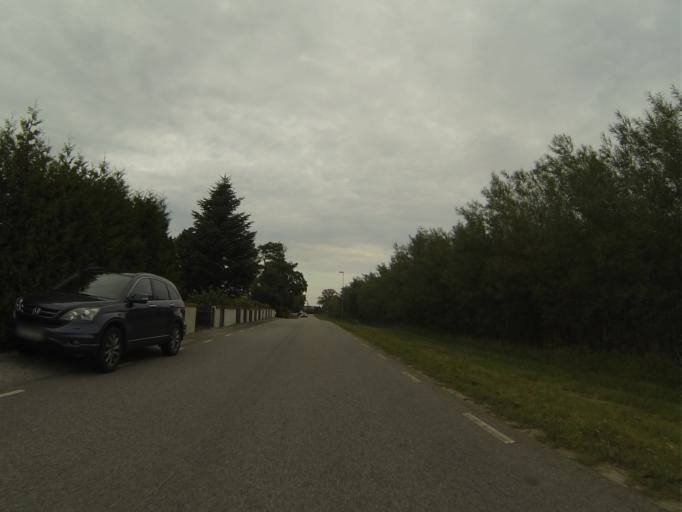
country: SE
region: Skane
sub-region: Staffanstorps Kommun
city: Hjaerup
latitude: 55.6398
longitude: 13.1460
